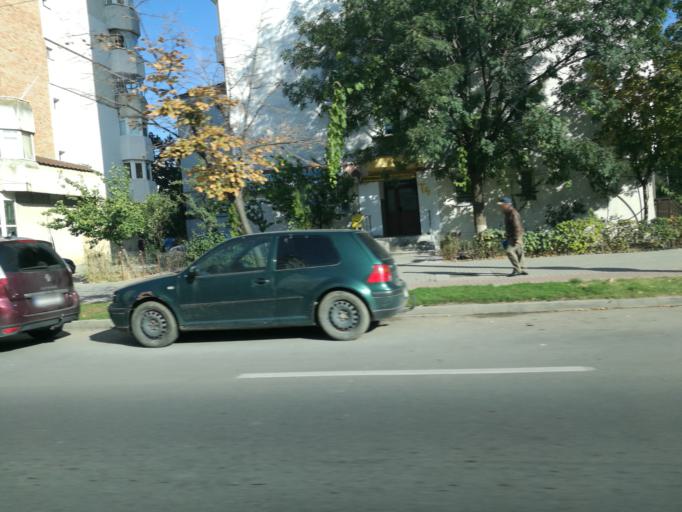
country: RO
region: Iasi
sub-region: Comuna Miroslava
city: Miroslava
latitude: 47.1748
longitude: 27.5452
